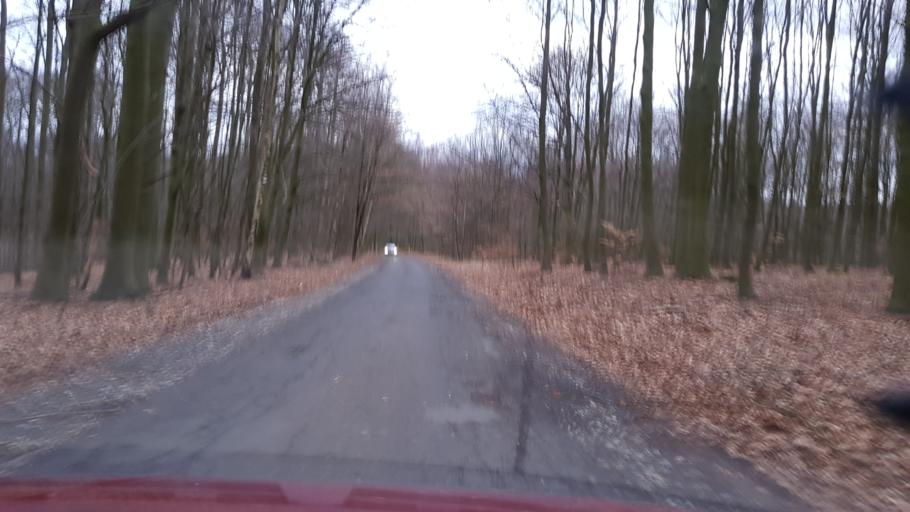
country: PL
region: West Pomeranian Voivodeship
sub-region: Powiat gryfinski
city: Stare Czarnowo
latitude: 53.3195
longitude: 14.7110
